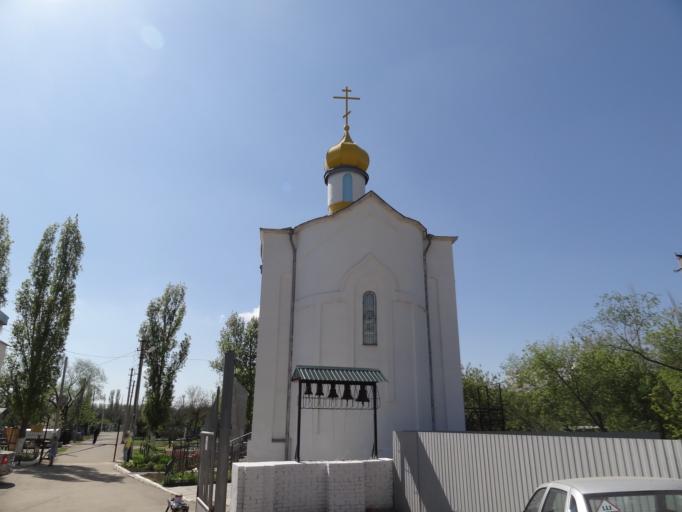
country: RU
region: Saratov
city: Engel's
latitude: 51.4714
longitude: 46.1332
